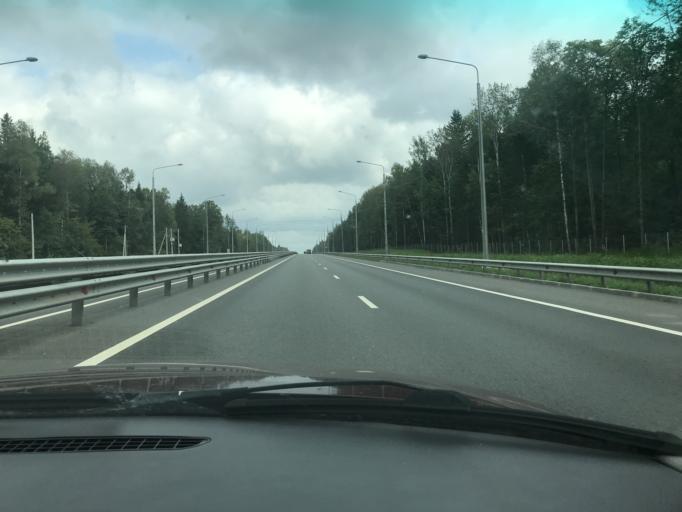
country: RU
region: Kaluga
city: Pyatovskiy
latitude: 54.6867
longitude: 36.1532
